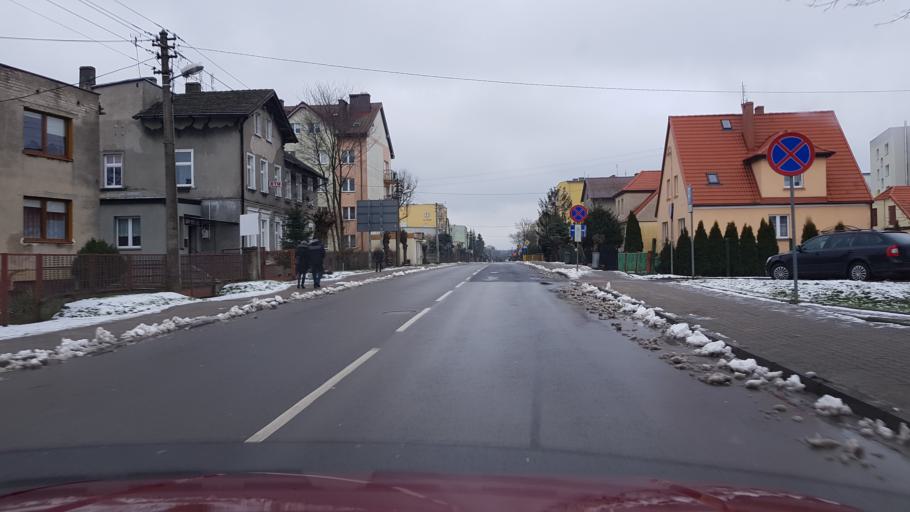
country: PL
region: West Pomeranian Voivodeship
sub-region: Powiat goleniowski
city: Nowogard
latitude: 53.6653
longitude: 15.1278
